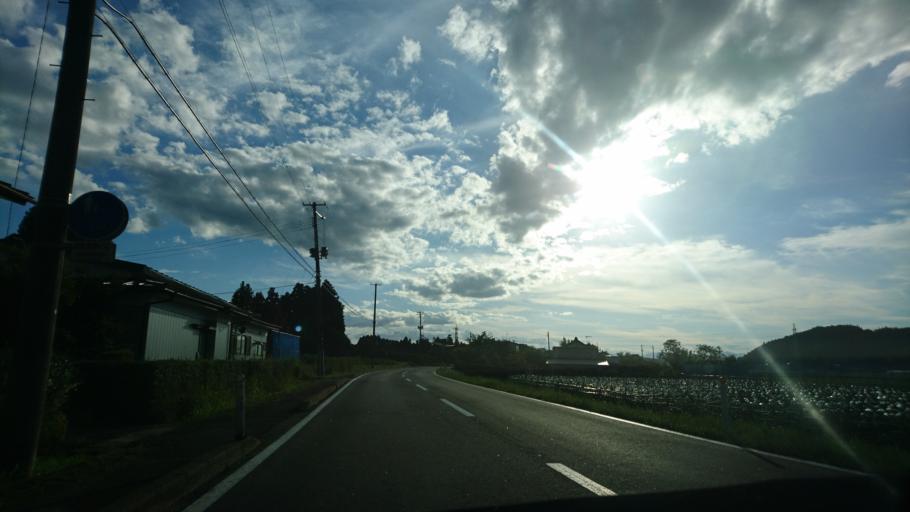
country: JP
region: Iwate
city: Ichinoseki
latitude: 38.8401
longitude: 141.1481
